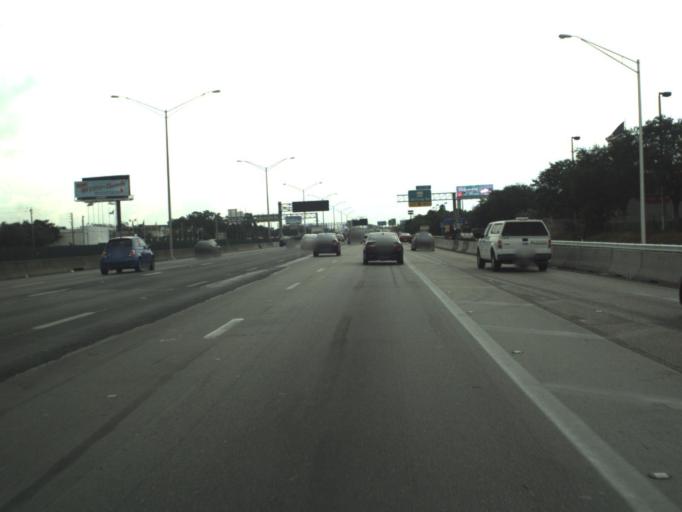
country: US
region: Florida
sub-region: Broward County
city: Dania Beach
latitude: 26.0373
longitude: -80.1635
